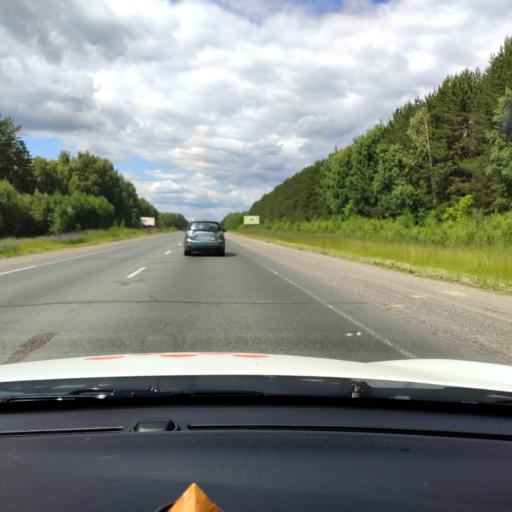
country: RU
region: Mariy-El
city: Pomary
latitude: 55.9320
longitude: 48.3733
